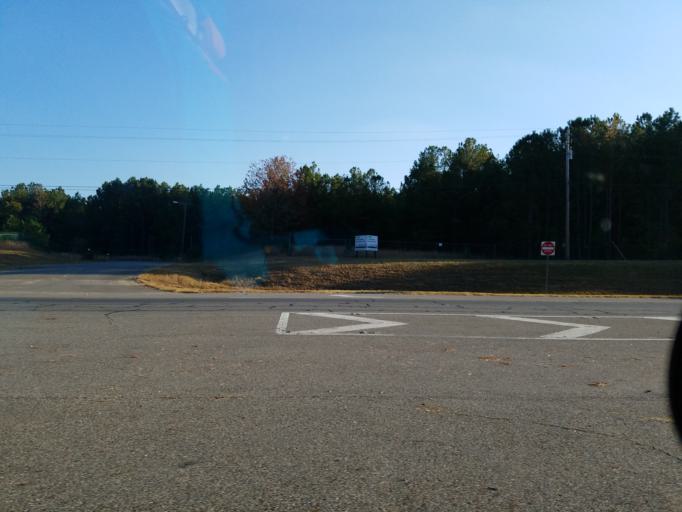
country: US
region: Georgia
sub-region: Bartow County
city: Euharlee
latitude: 34.2202
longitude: -84.9171
